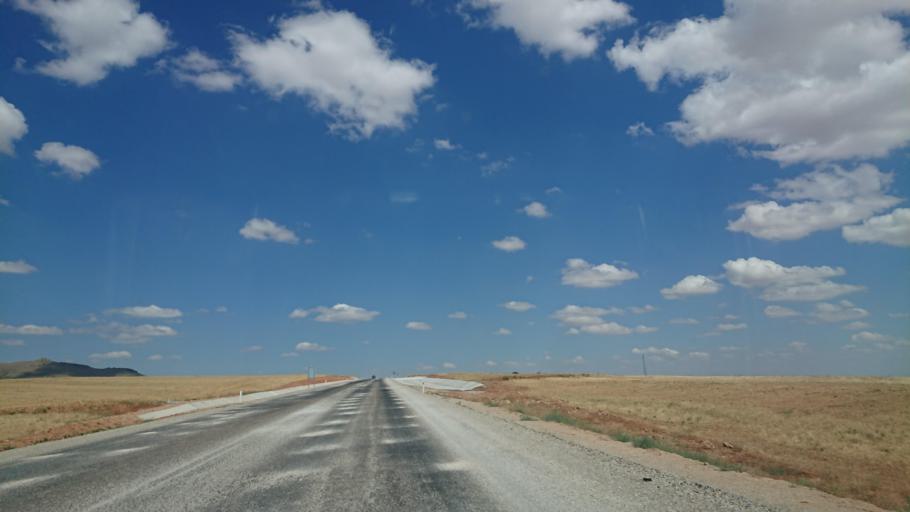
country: TR
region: Kirsehir
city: Kirsehir
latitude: 39.1237
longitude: 33.9737
